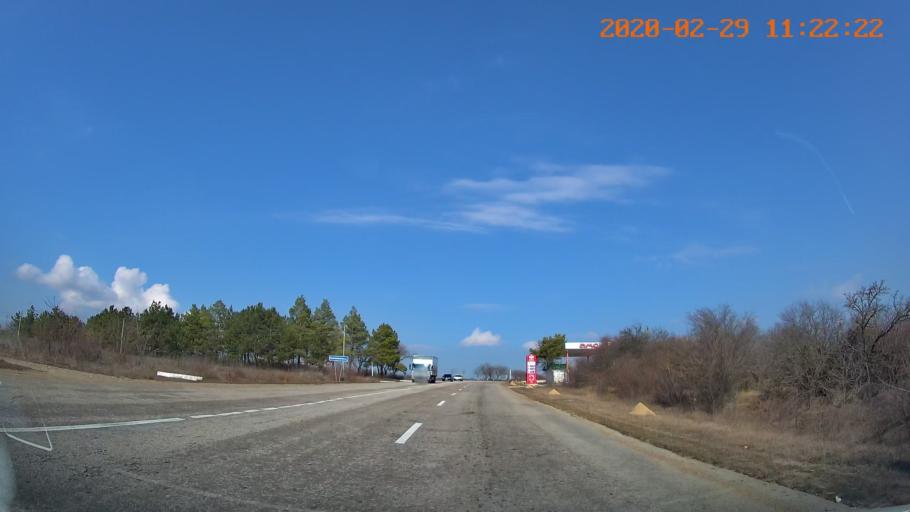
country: MD
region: Telenesti
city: Cocieri
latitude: 47.3931
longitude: 29.1623
